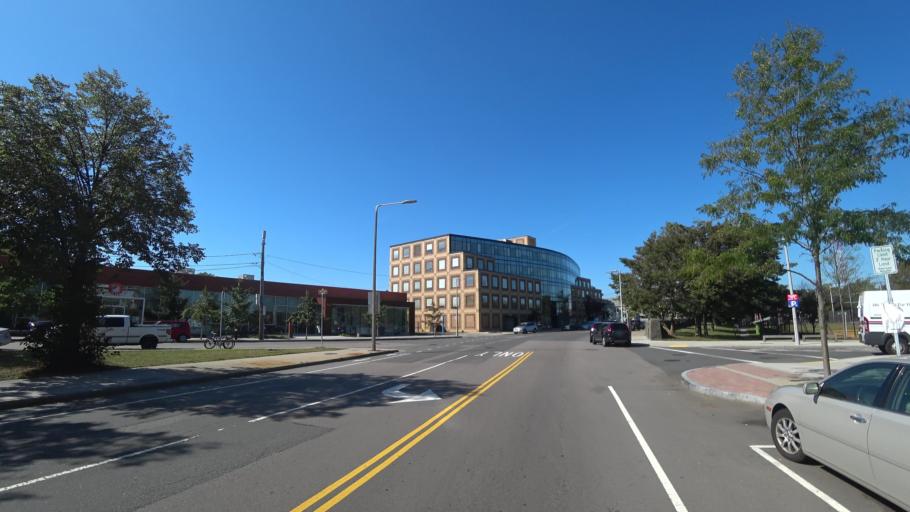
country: US
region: Massachusetts
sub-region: Middlesex County
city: Cambridge
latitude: 42.3632
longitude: -71.1308
